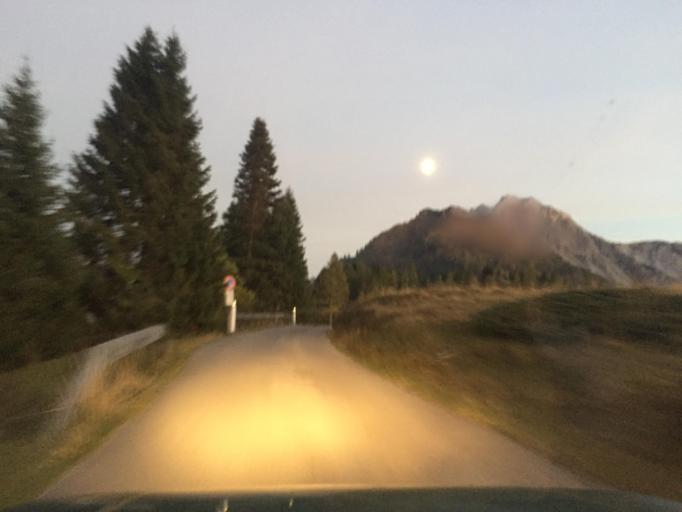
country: IT
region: Veneto
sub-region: Provincia di Belluno
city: Granvilla
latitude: 46.6178
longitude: 12.7212
